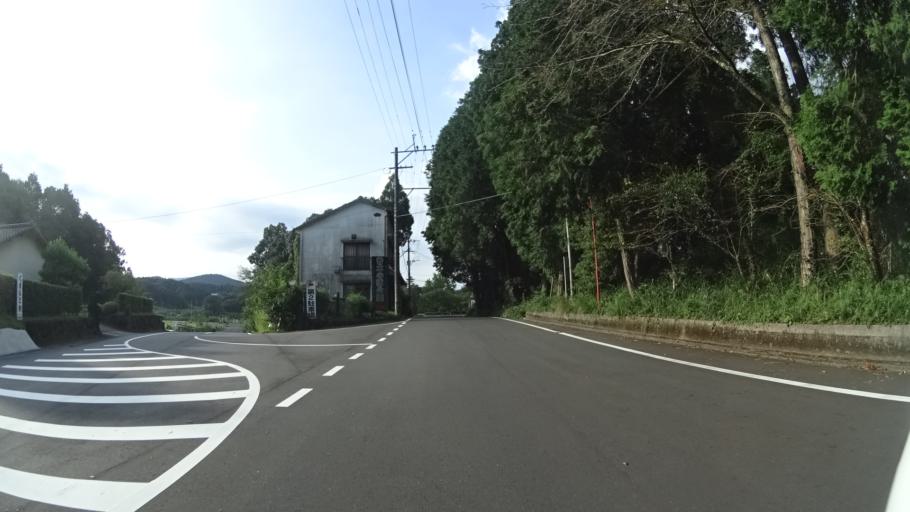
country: JP
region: Kagoshima
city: Okuchi-shinohara
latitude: 32.0141
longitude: 130.5772
